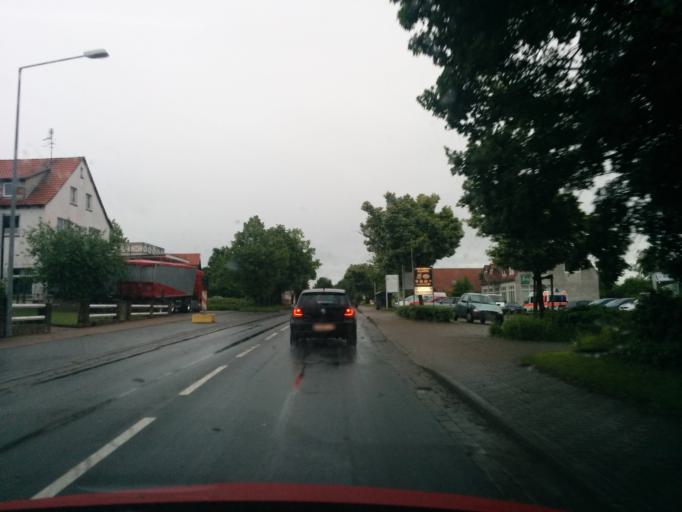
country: DE
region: Lower Saxony
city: Gieboldehausen
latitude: 51.6153
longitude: 10.2187
